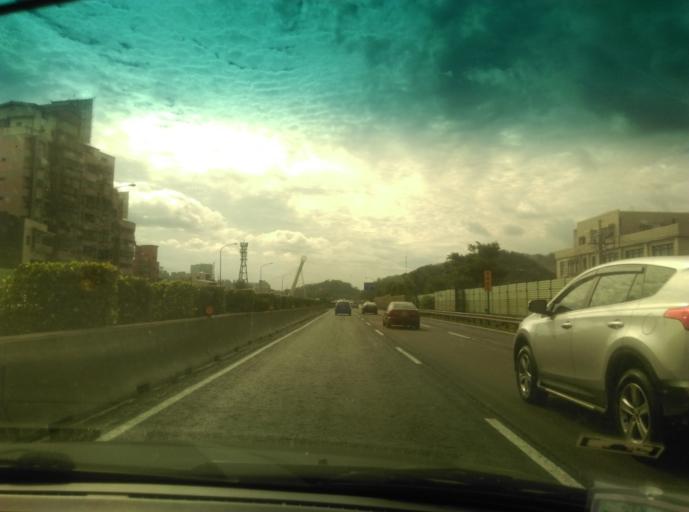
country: TW
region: Taiwan
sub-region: Keelung
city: Keelung
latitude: 25.0816
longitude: 121.6682
